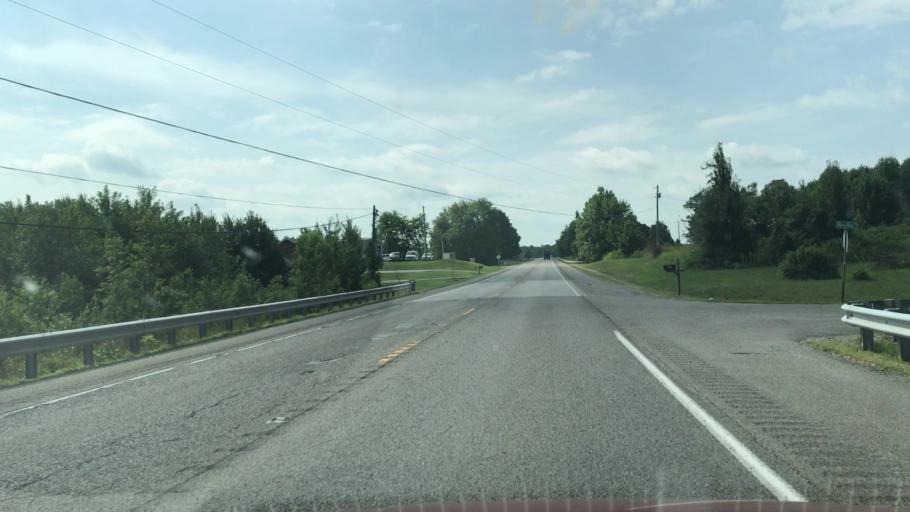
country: US
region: Kentucky
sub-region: Barren County
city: Glasgow
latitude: 37.0565
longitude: -85.9538
